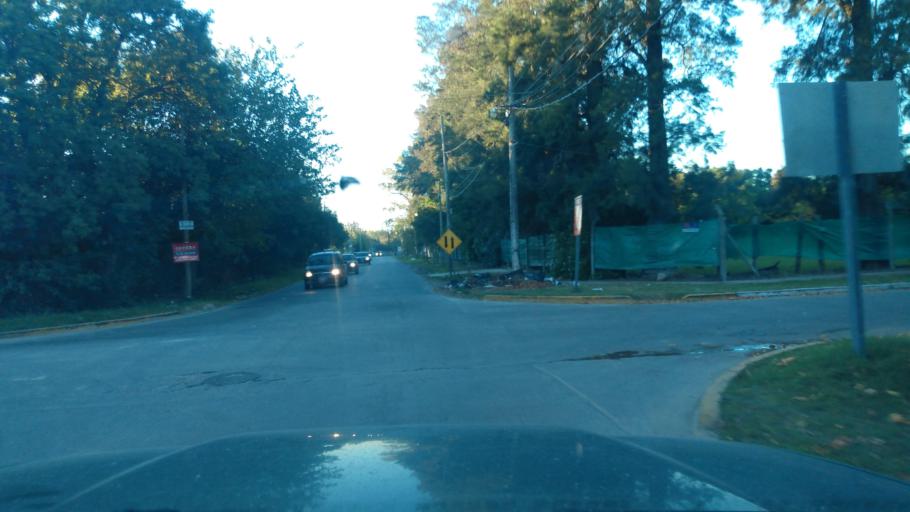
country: AR
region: Buenos Aires
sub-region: Partido de Merlo
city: Merlo
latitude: -34.6595
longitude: -58.7497
